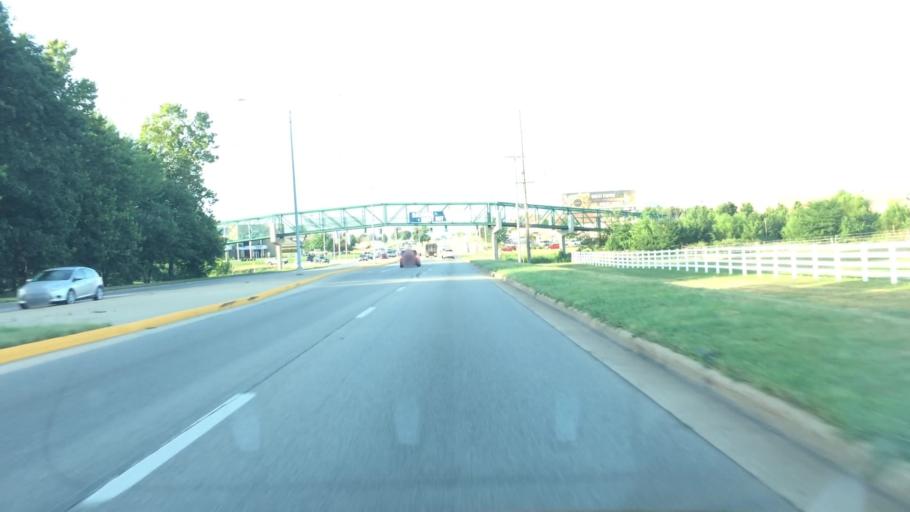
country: US
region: Missouri
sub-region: Greene County
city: Springfield
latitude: 37.1688
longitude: -93.3162
